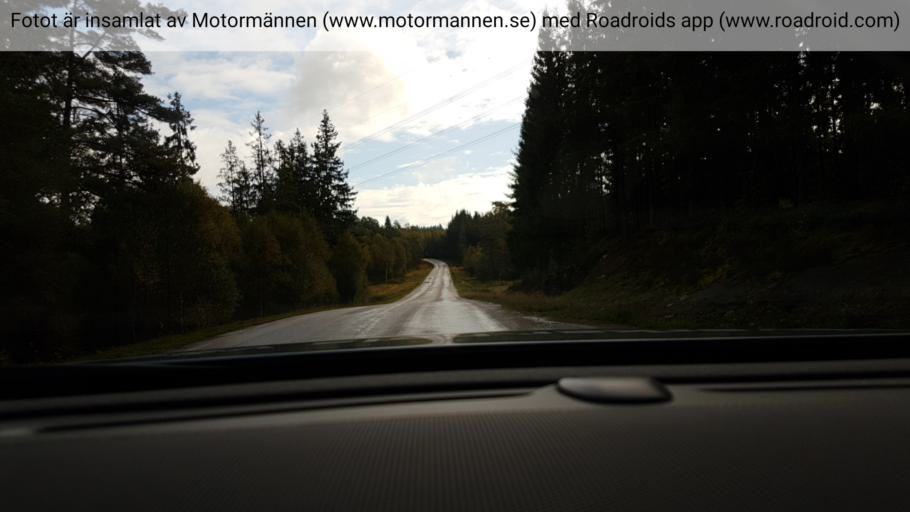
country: SE
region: Vaestra Goetaland
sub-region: Marks Kommun
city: Fritsla
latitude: 57.4021
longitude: 12.8716
